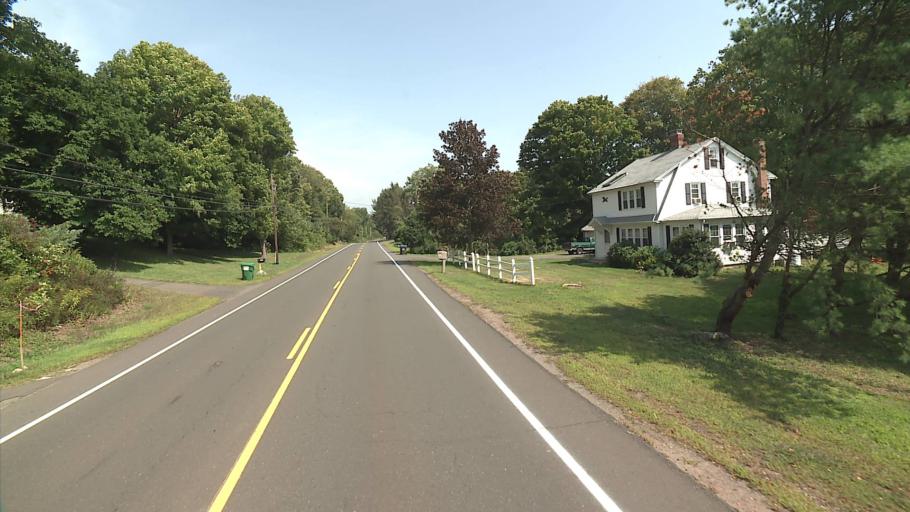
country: US
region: Connecticut
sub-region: Middlesex County
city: Durham
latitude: 41.4163
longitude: -72.6562
